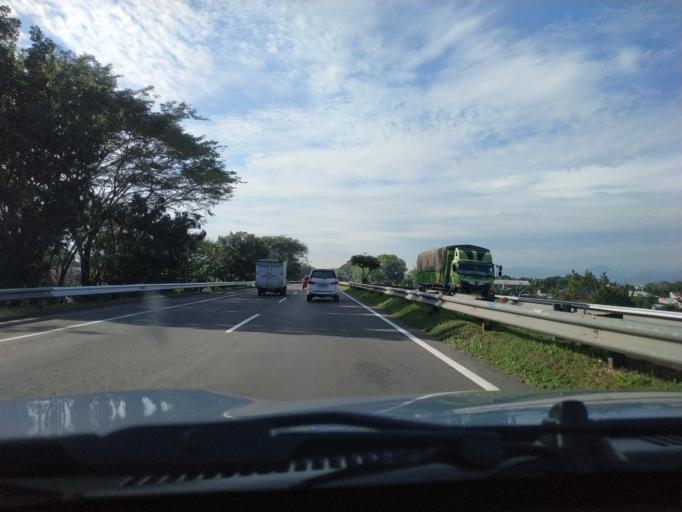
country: ID
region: North Sumatra
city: Medan
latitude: 3.5806
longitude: 98.7245
